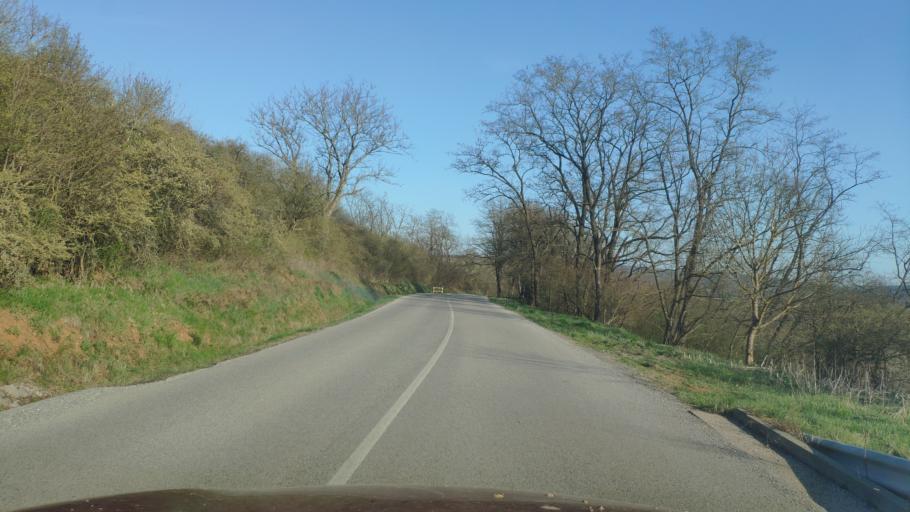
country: SK
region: Banskobystricky
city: Revuca
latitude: 48.4989
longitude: 20.2581
